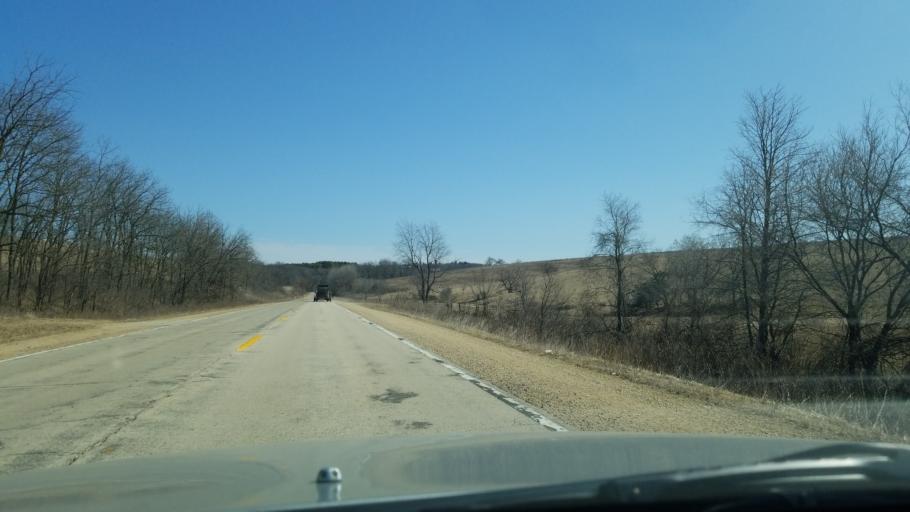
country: US
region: Wisconsin
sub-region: Iowa County
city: Mineral Point
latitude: 42.8793
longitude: -90.2177
